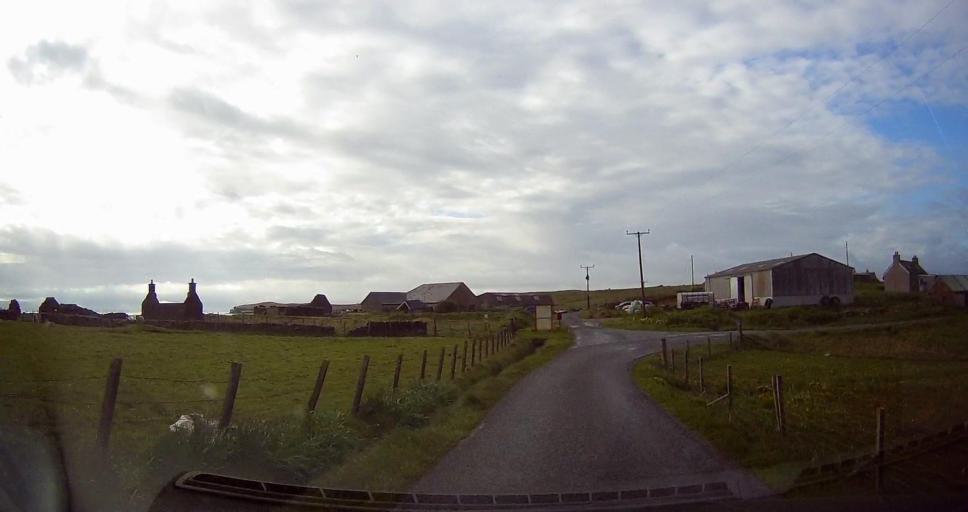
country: GB
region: Scotland
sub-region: Shetland Islands
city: Sandwick
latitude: 60.0505
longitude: -1.2061
